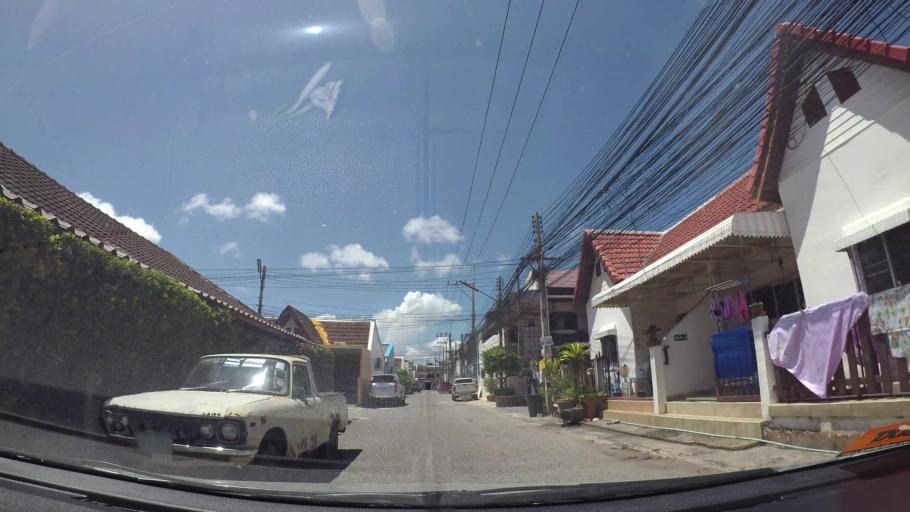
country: TH
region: Chon Buri
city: Phatthaya
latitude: 12.9257
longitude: 100.8858
